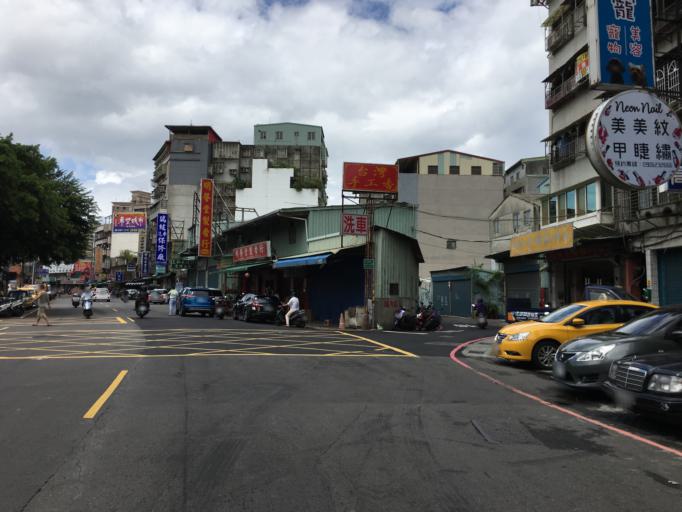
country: TW
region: Taipei
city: Taipei
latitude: 25.0812
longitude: 121.4907
